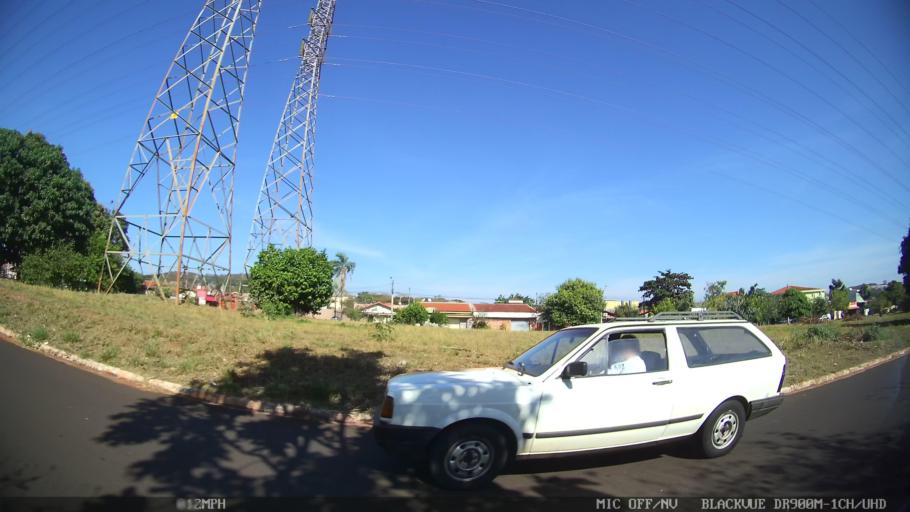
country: BR
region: Sao Paulo
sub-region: Ribeirao Preto
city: Ribeirao Preto
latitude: -21.2229
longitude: -47.7632
